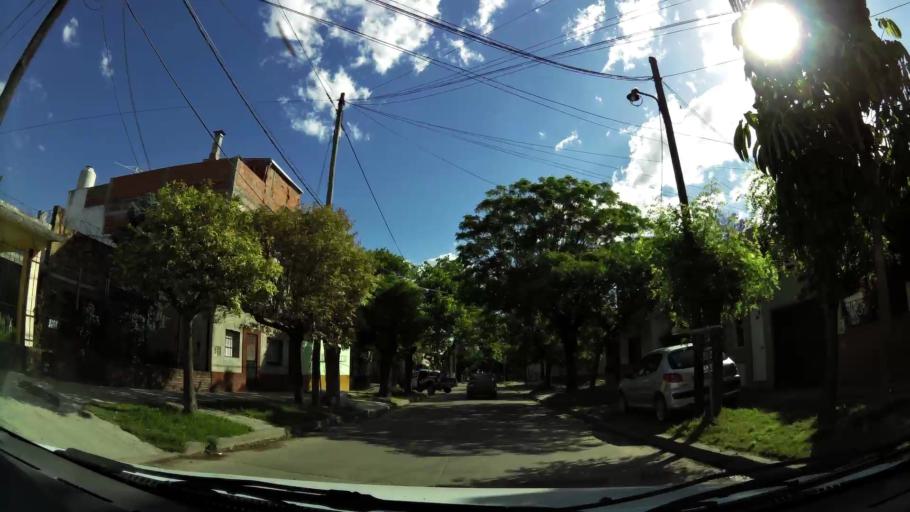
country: AR
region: Buenos Aires
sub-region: Partido de General San Martin
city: General San Martin
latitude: -34.5256
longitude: -58.5792
